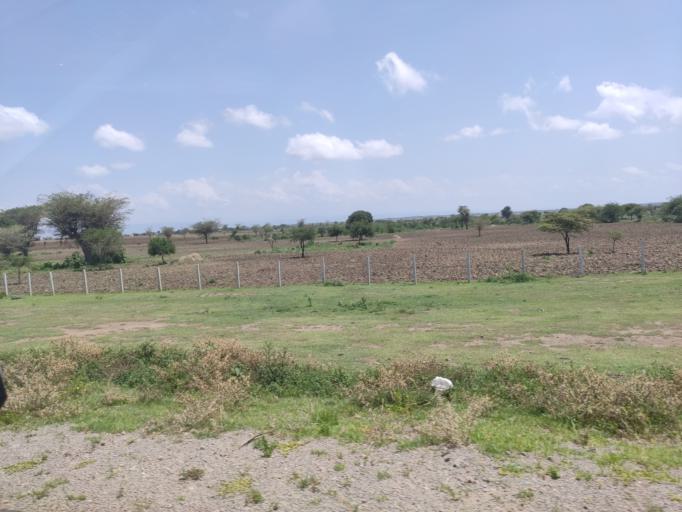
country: ET
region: Oromiya
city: Ziway
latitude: 8.2574
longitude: 38.8962
